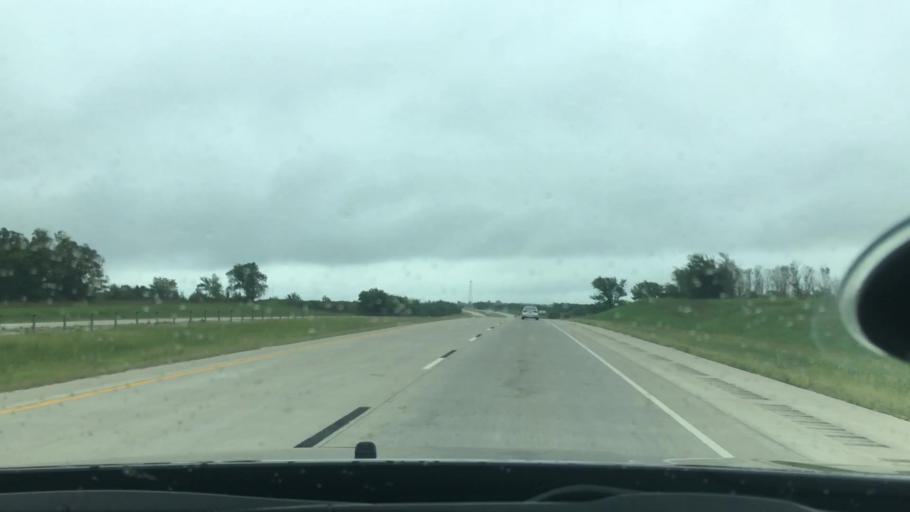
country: US
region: Oklahoma
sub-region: Okmulgee County
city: Wilson
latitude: 35.4273
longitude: -96.0748
